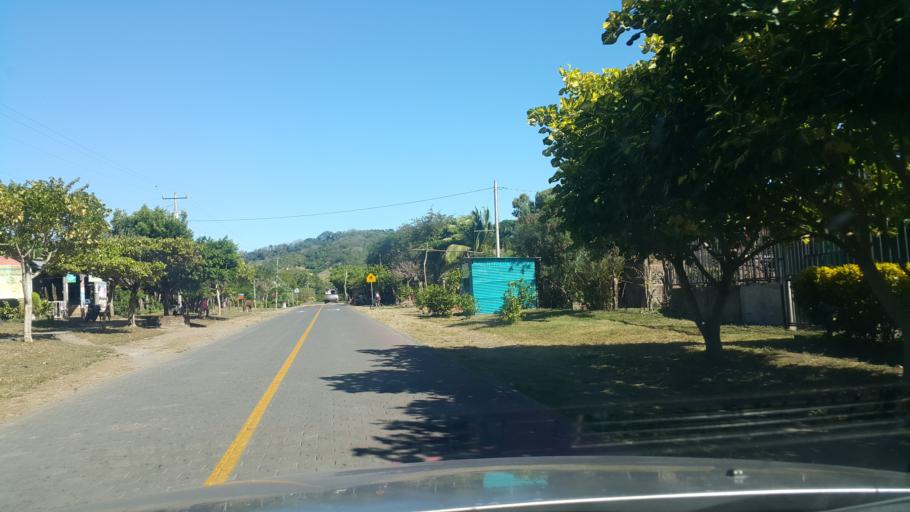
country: NI
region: Rivas
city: Moyogalpa
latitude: 11.4858
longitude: -85.6426
